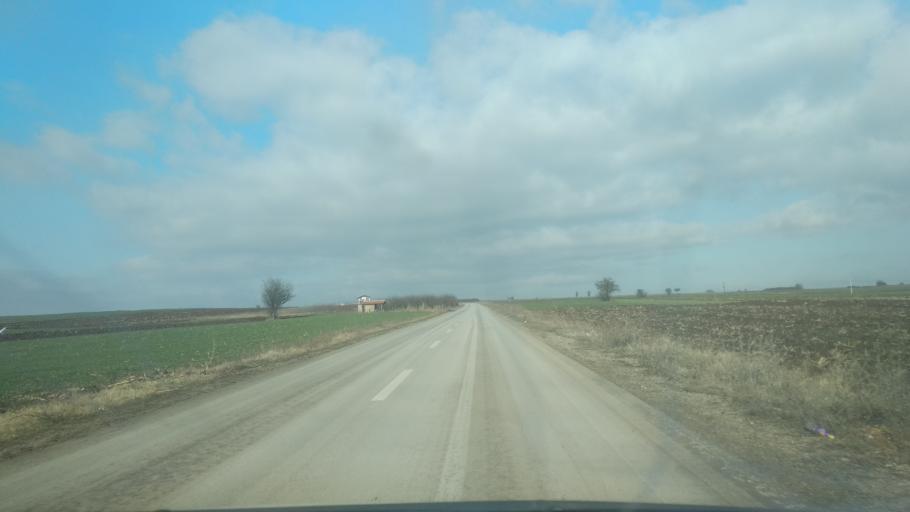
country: XK
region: Pristina
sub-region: Lipjan
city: Lipljan
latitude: 42.5534
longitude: 21.1770
